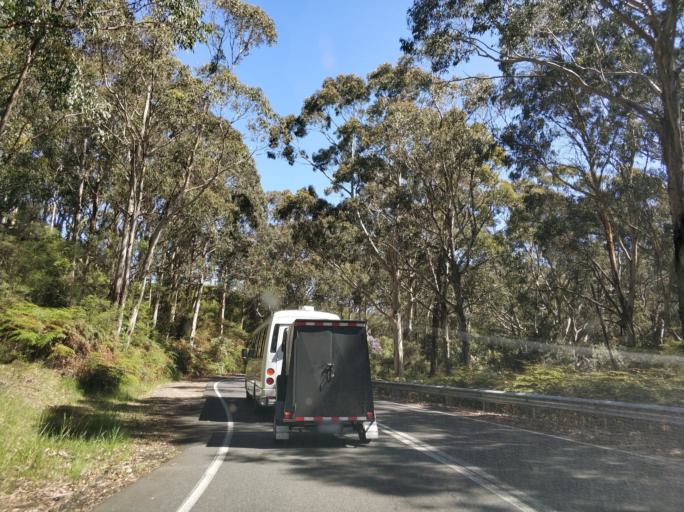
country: AU
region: Victoria
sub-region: Colac-Otway
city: Apollo Bay
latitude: -38.7459
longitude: 143.2737
